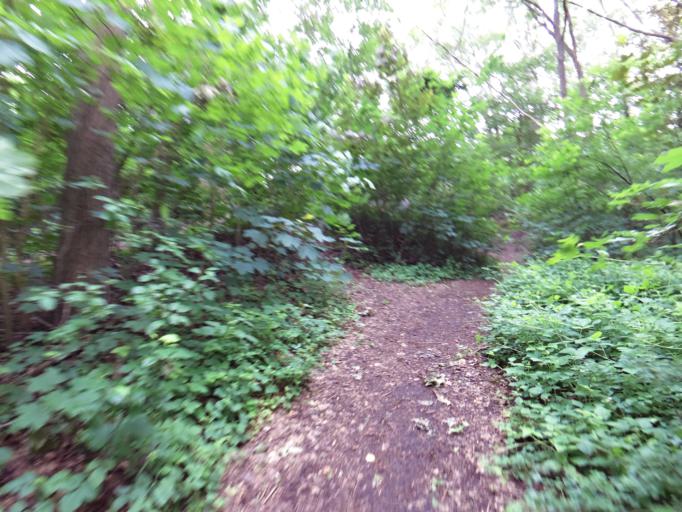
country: NL
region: South Holland
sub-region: Gemeente Hellevoetsluis
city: Nieuw-Helvoet
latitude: 51.8701
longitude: 4.0568
